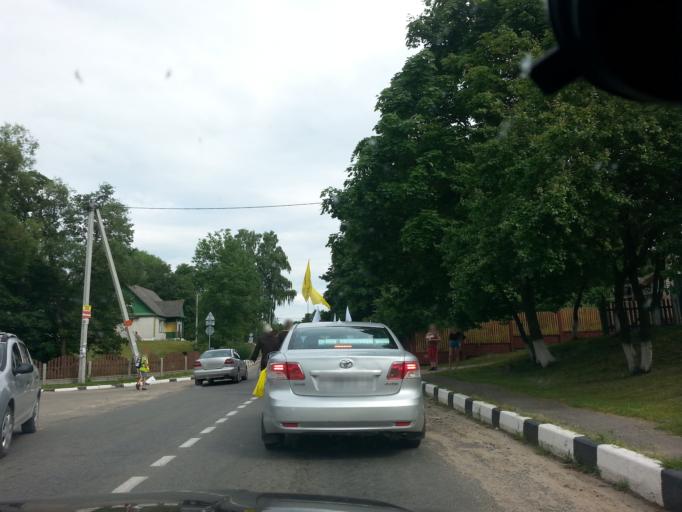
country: BY
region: Minsk
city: Narach
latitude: 54.8902
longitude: 26.7758
